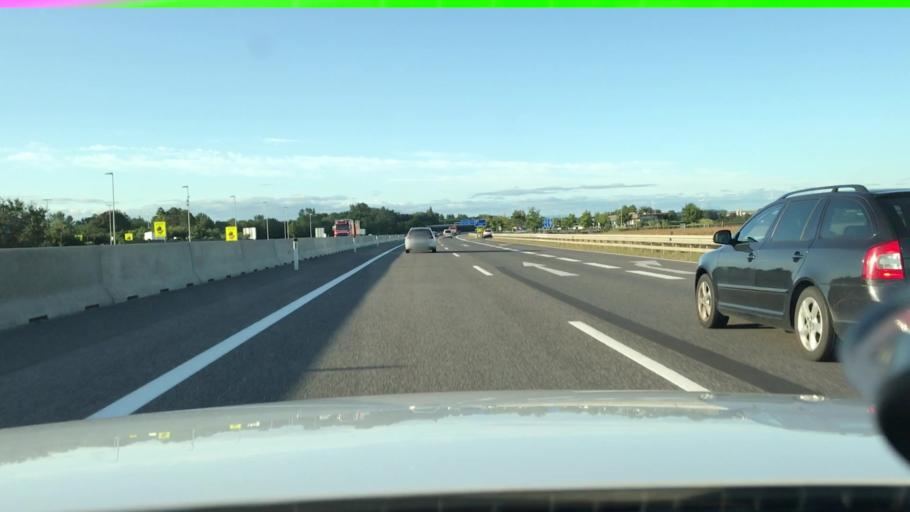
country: AT
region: Lower Austria
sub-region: Politischer Bezirk Sankt Polten
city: Herzogenburg
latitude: 48.3135
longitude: 15.7167
